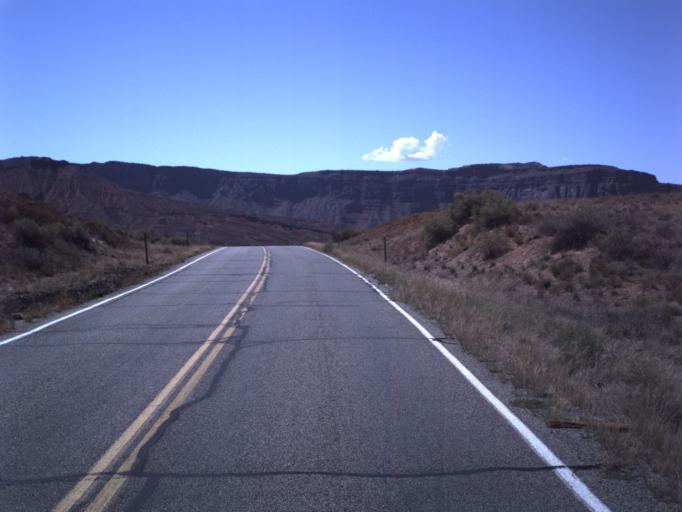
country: US
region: Utah
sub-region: Grand County
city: Moab
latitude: 38.6917
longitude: -109.4119
